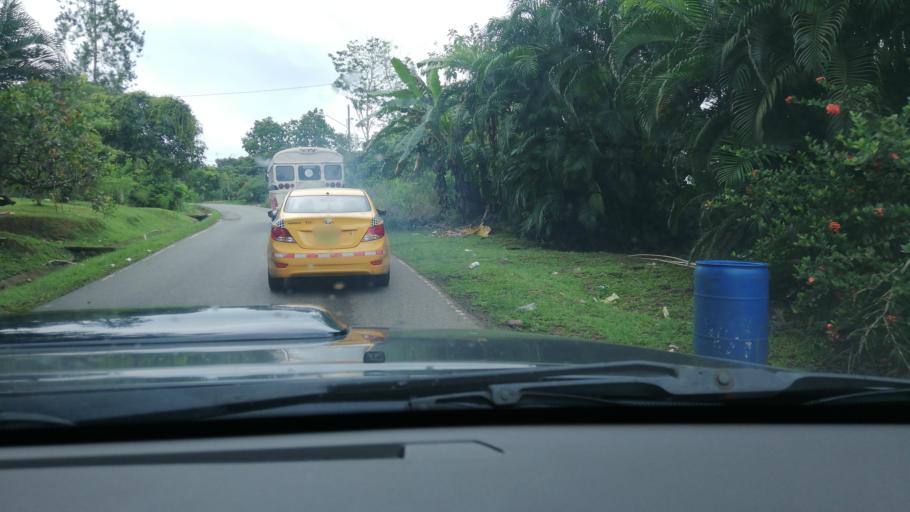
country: PA
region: Panama
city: San Miguelito
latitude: 9.0964
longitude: -79.4482
